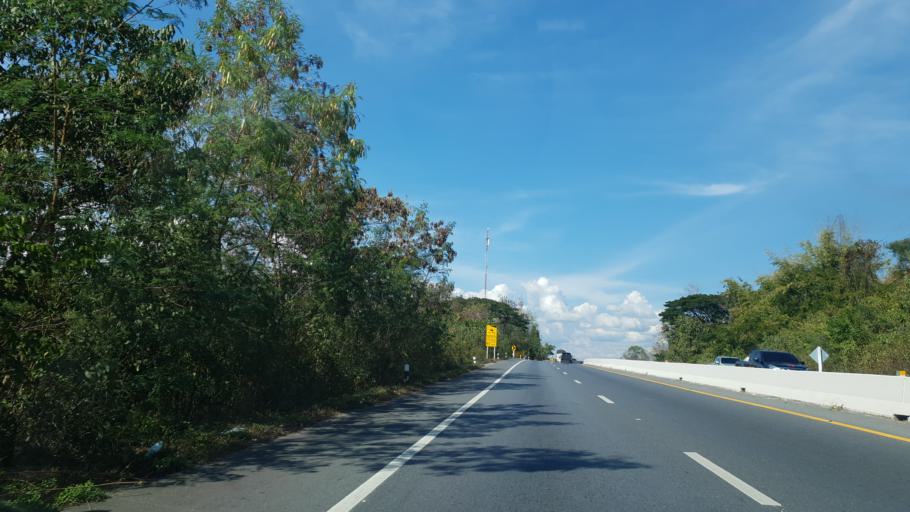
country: TH
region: Phrae
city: Den Chai
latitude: 17.9331
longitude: 100.0621
